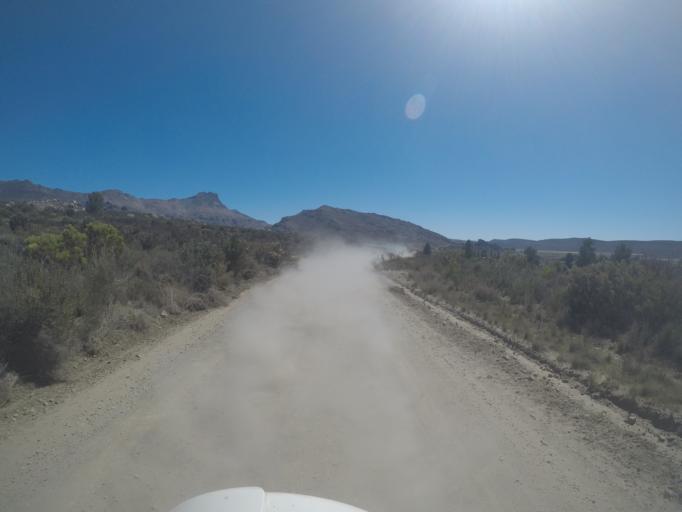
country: ZA
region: Western Cape
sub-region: Cape Winelands District Municipality
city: Ceres
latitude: -32.8705
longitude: 19.4439
